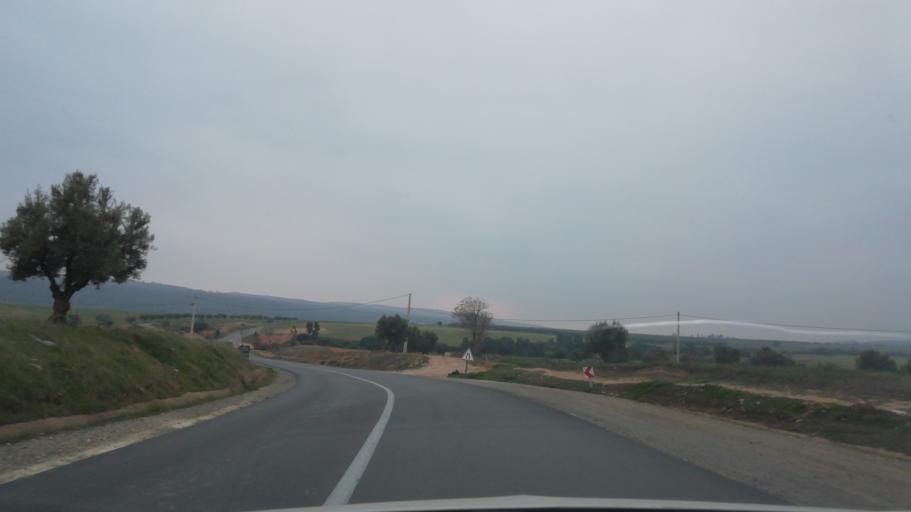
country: DZ
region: Sidi Bel Abbes
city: Sfizef
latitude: 35.2764
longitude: -0.1548
